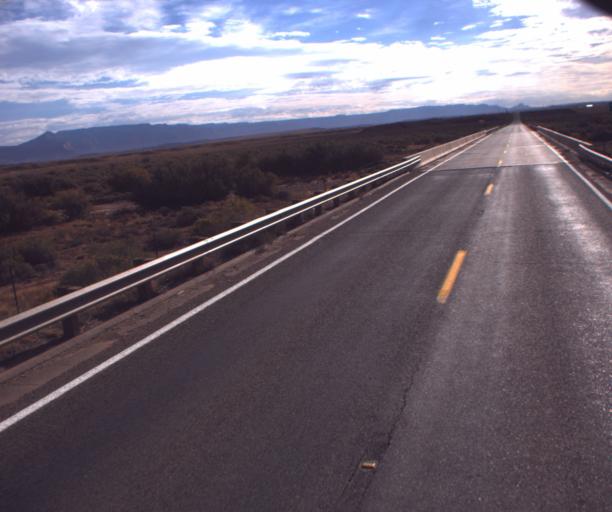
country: US
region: Arizona
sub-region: Apache County
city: Many Farms
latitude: 36.5311
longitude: -109.5078
